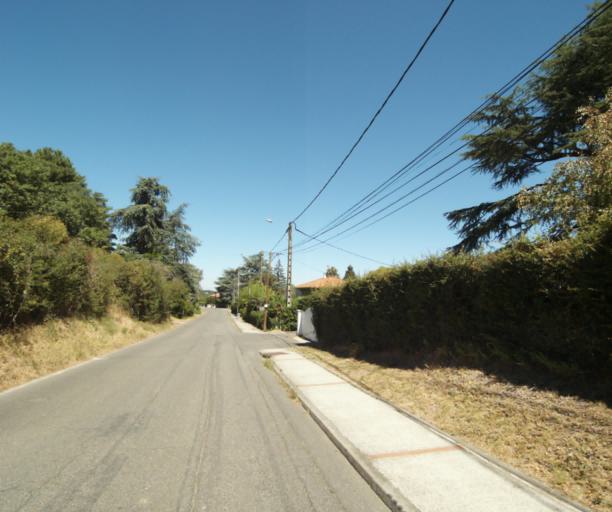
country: FR
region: Midi-Pyrenees
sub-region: Departement de la Haute-Garonne
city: Castanet-Tolosan
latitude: 43.5087
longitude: 1.4985
